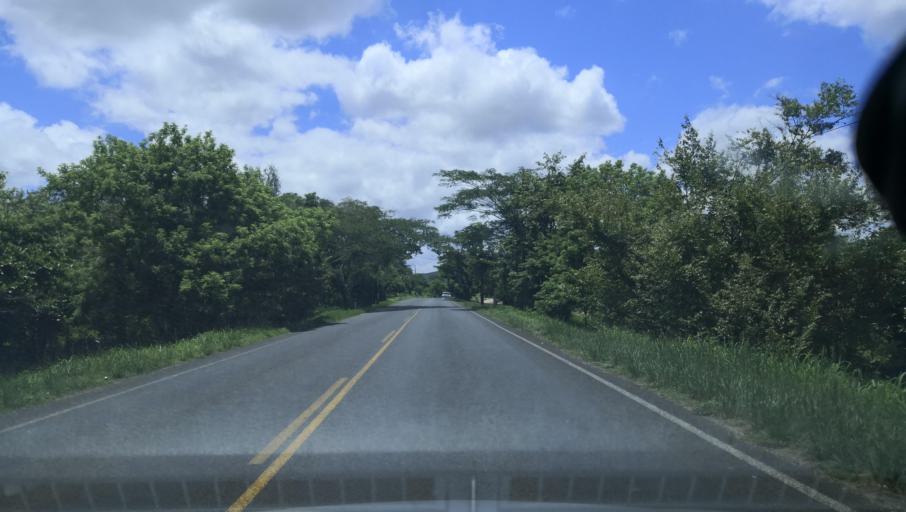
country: NI
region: Esteli
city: Condega
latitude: 13.2334
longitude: -86.3776
